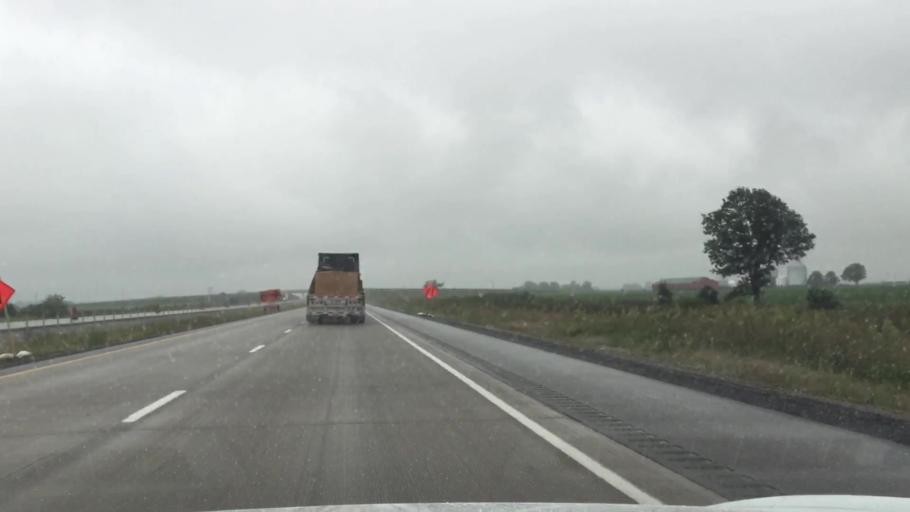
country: CA
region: Ontario
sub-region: Lambton County
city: Walpole Island
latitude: 42.3055
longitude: -82.3204
